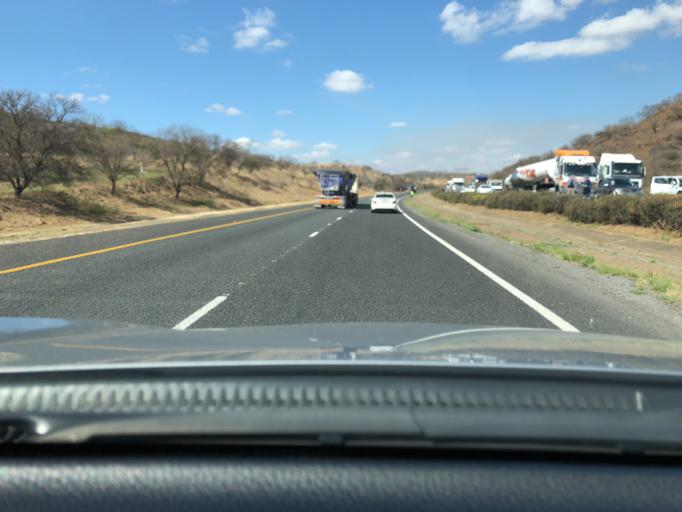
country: ZA
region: KwaZulu-Natal
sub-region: uThukela District Municipality
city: Ladysmith
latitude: -28.7182
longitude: 29.6472
